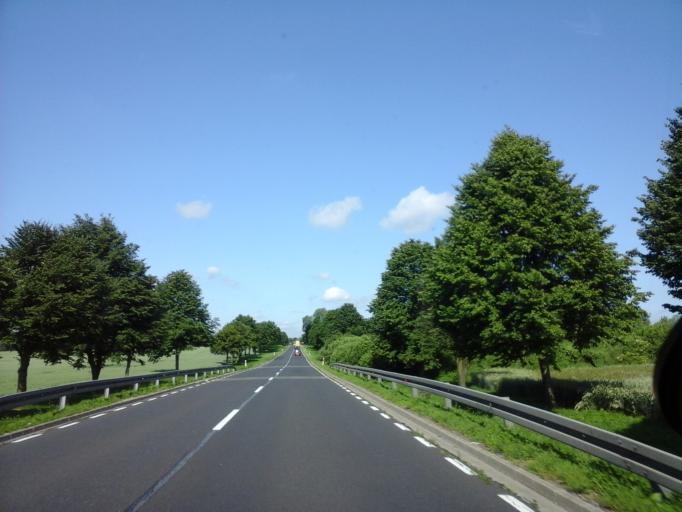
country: PL
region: West Pomeranian Voivodeship
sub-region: Powiat choszczenski
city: Recz
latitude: 53.2725
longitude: 15.4813
